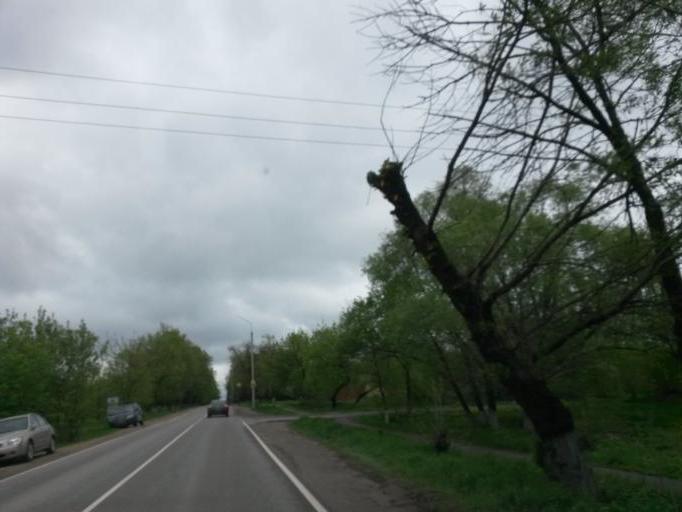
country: RU
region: Moskovskaya
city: Klimovsk
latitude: 55.3489
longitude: 37.5466
